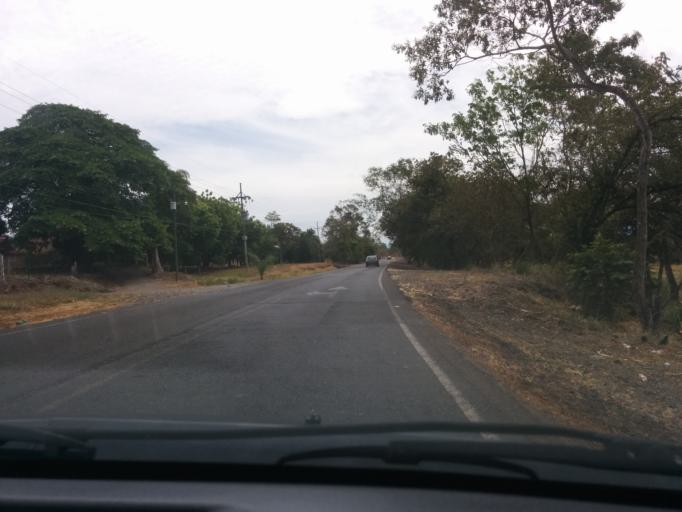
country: CR
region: Puntarenas
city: Esparza
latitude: 10.0051
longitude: -84.6287
